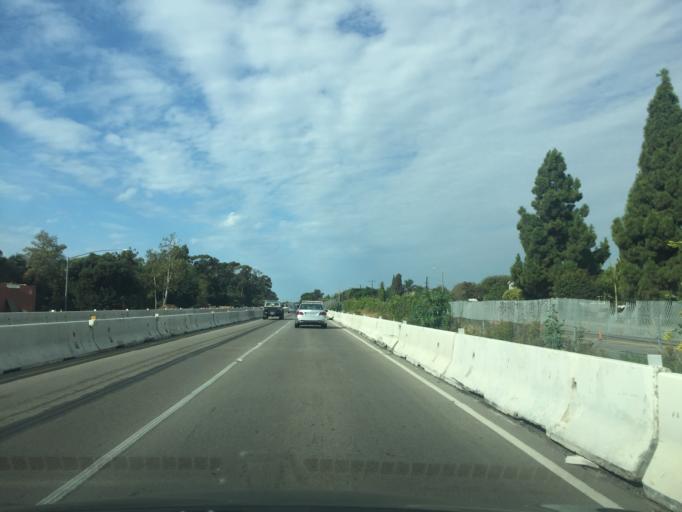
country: US
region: California
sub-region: Santa Barbara County
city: Goleta
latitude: 34.4394
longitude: -119.8353
